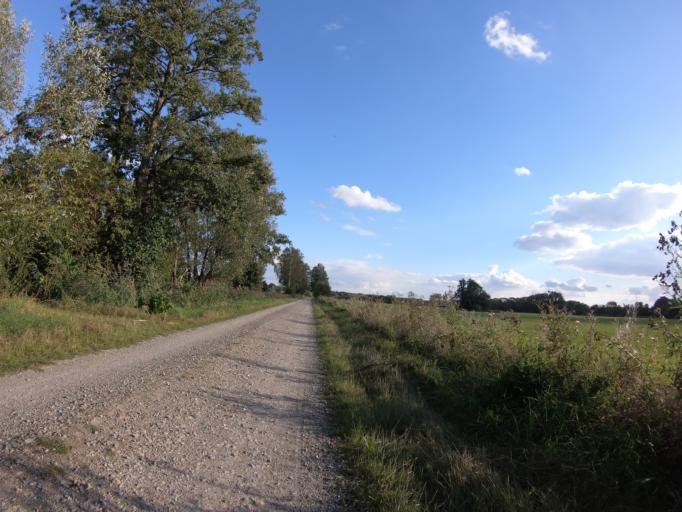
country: DE
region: Lower Saxony
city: Osloss
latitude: 52.4337
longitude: 10.6719
